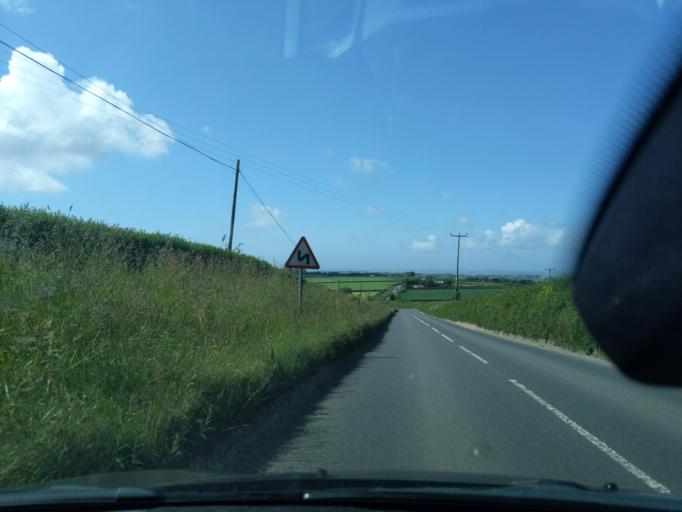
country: GB
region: England
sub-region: Devon
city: Great Torrington
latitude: 50.9925
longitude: -4.0949
